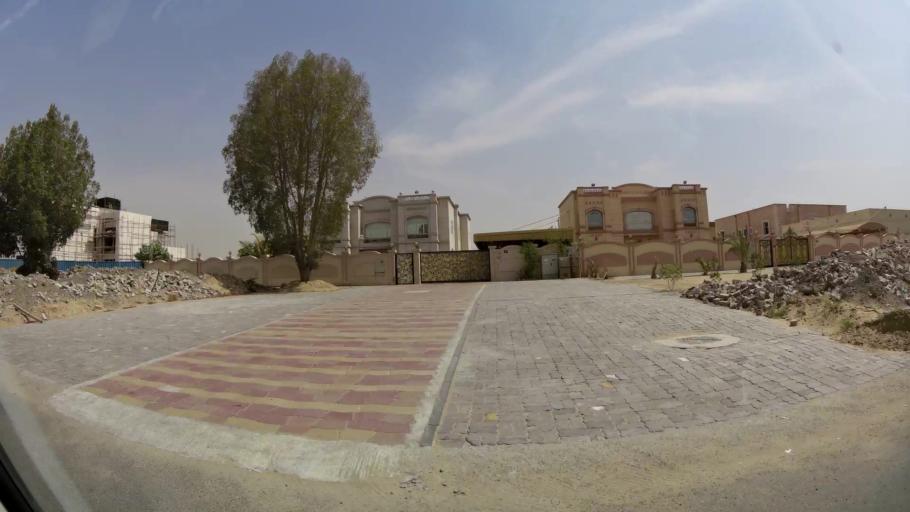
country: AE
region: Ash Shariqah
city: Sharjah
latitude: 25.2507
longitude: 55.4744
